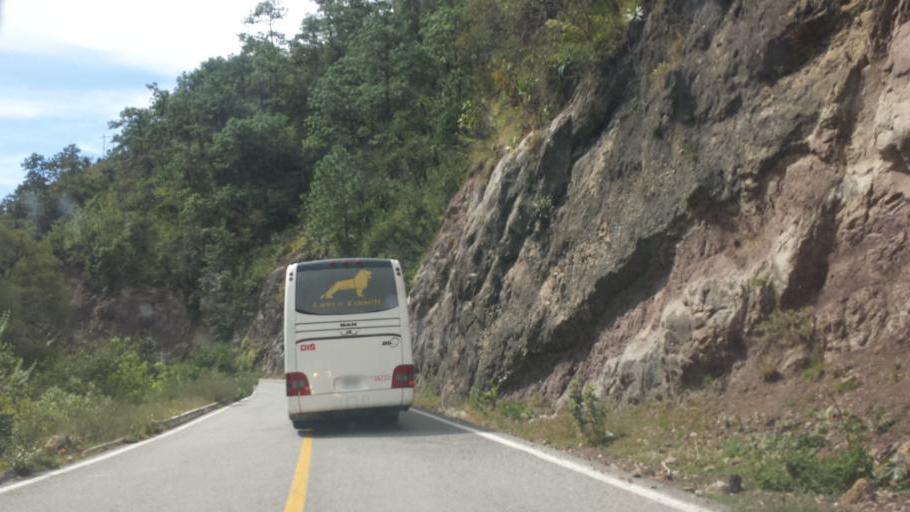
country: MX
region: Oaxaca
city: San Francisco Sola
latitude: 16.4450
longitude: -97.0331
